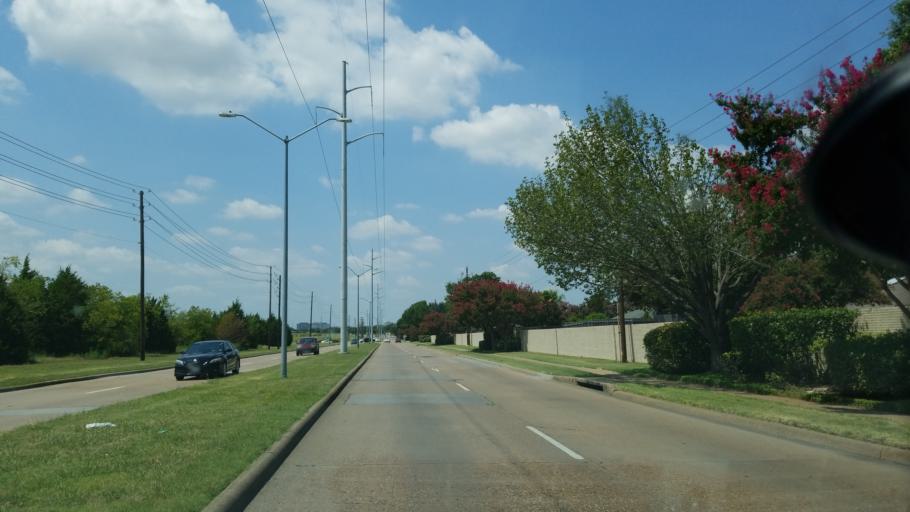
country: US
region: Texas
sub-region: Dallas County
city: Richardson
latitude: 32.9254
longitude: -96.7270
